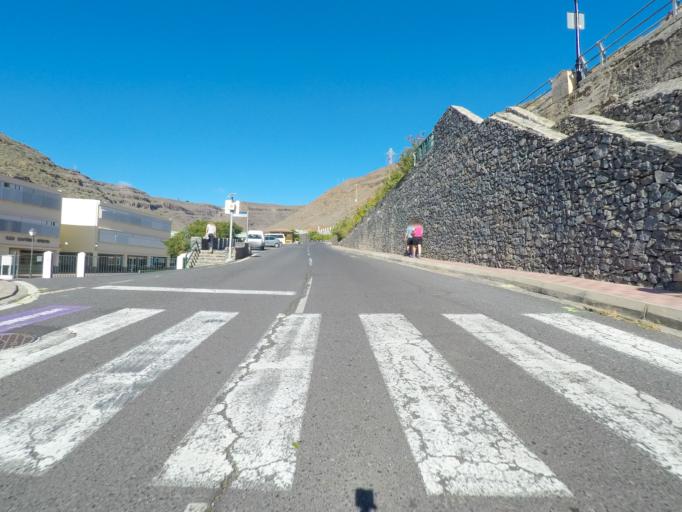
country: ES
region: Canary Islands
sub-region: Provincia de Santa Cruz de Tenerife
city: Alajero
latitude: 28.0320
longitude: -17.1994
